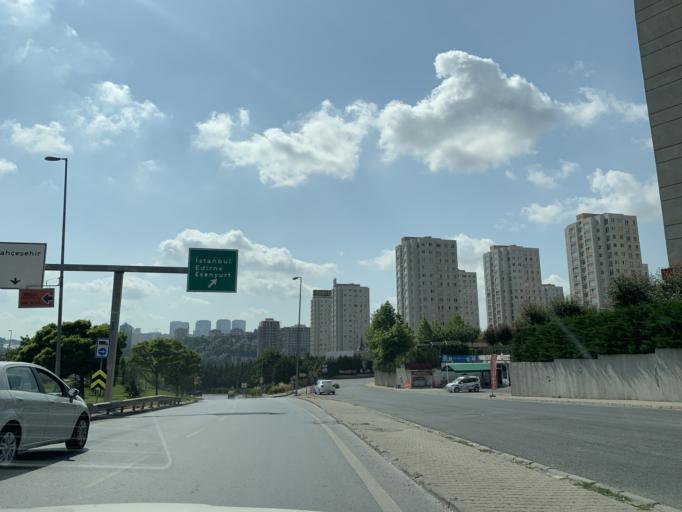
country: TR
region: Istanbul
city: Esenyurt
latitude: 41.0599
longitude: 28.7068
